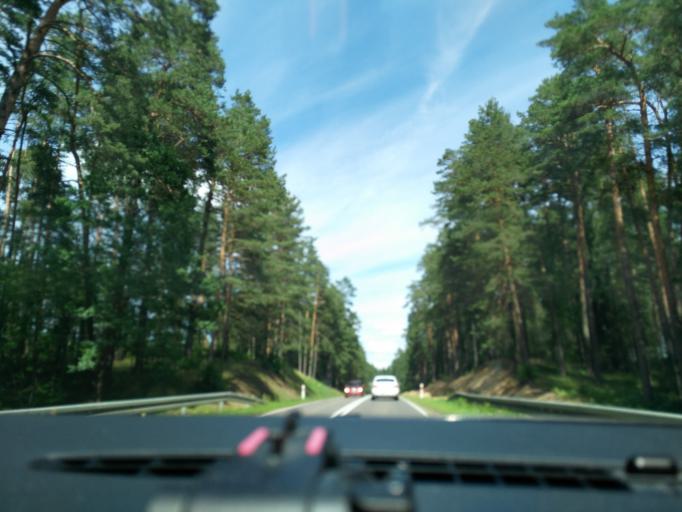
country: PL
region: Podlasie
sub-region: Powiat augustowski
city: Augustow
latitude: 53.8501
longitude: 23.0486
